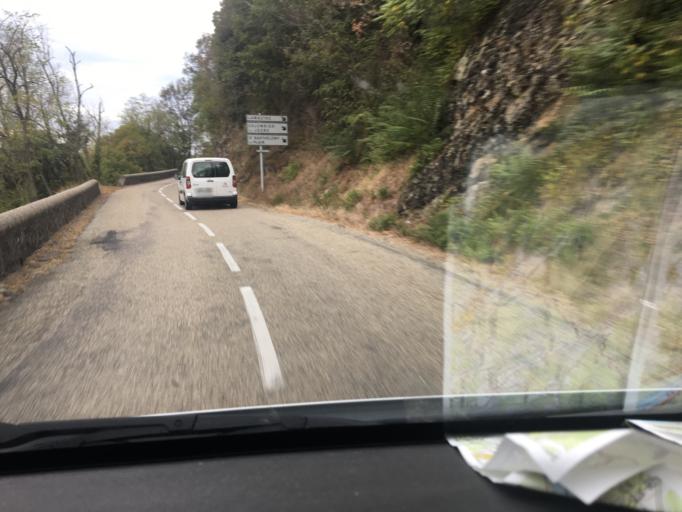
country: FR
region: Rhone-Alpes
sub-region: Departement de l'Ardeche
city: Saint-Jean-de-Muzols
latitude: 45.0610
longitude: 4.7483
